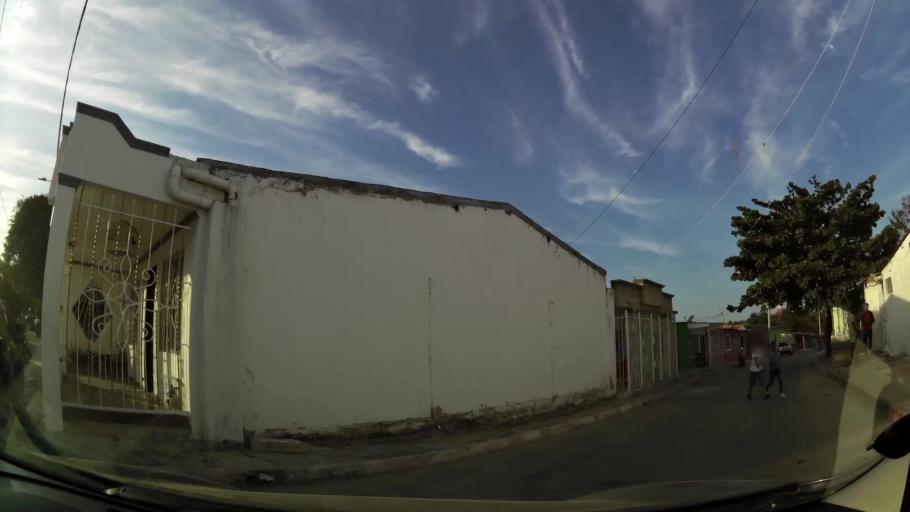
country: CO
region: Atlantico
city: Barranquilla
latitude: 10.9571
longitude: -74.8193
